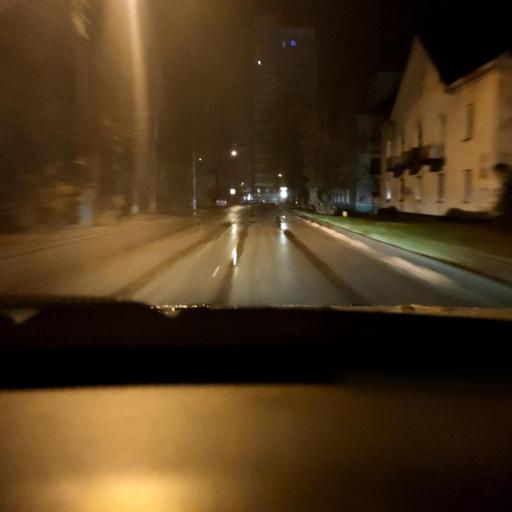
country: RU
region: Perm
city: Kultayevo
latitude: 58.0010
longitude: 55.9548
